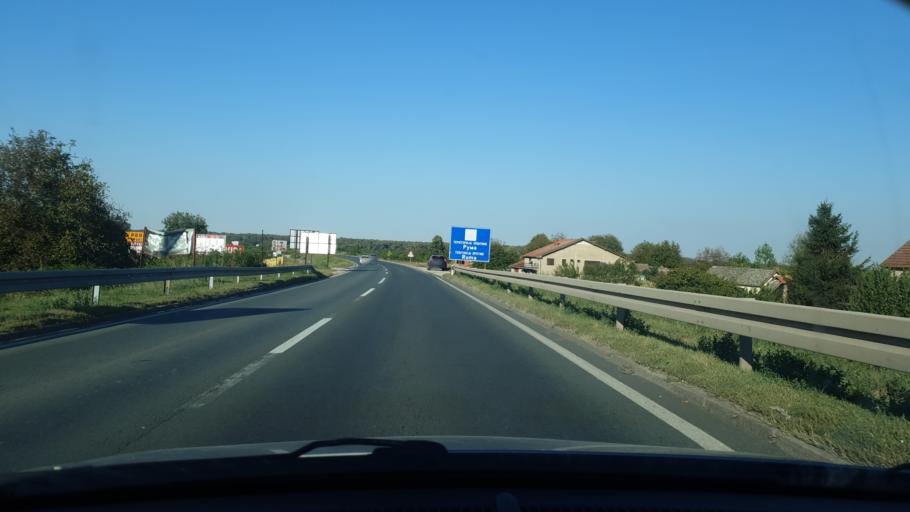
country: RS
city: Klenak
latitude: 44.7600
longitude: 19.7206
